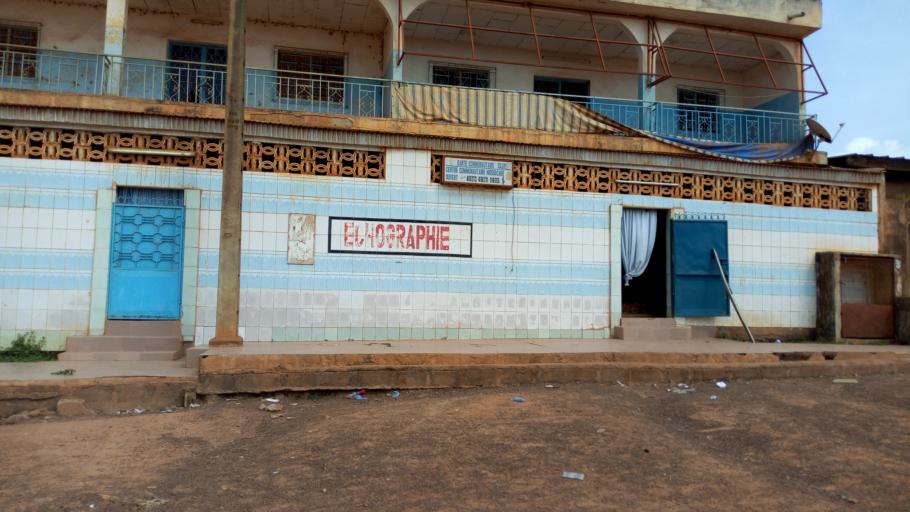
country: CI
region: Vallee du Bandama
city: Bouake
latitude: 7.7259
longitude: -5.0318
